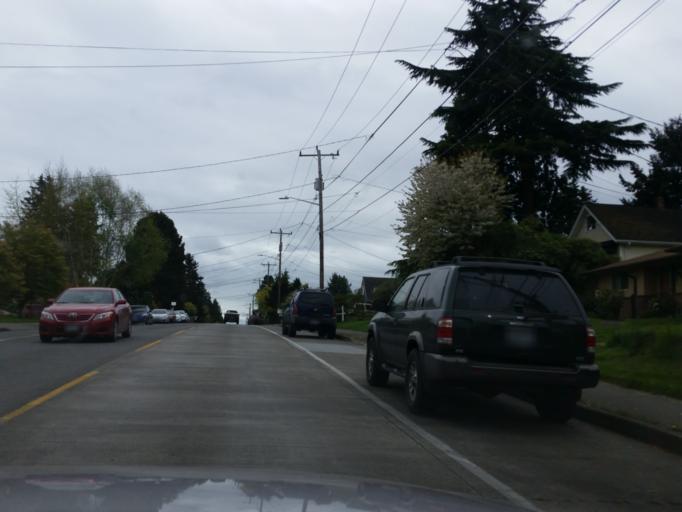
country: US
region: Washington
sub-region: King County
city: Shoreline
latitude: 47.6955
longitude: -122.3661
